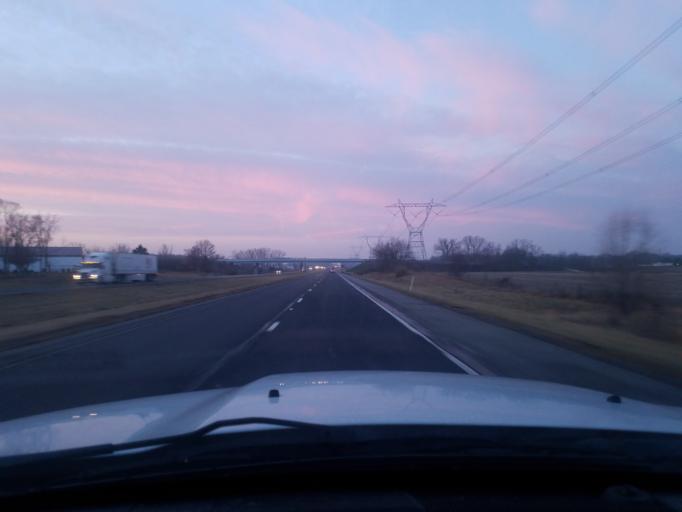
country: US
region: Indiana
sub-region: Huntington County
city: Roanoke
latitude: 40.9336
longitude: -85.3124
